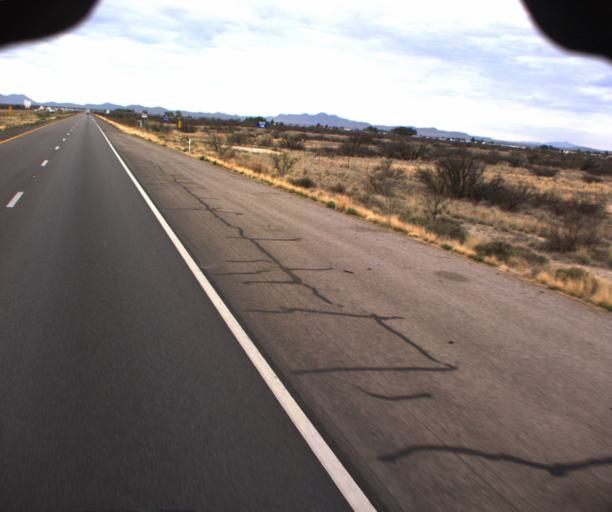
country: US
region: Arizona
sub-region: Cochise County
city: Willcox
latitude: 32.2608
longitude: -109.8485
